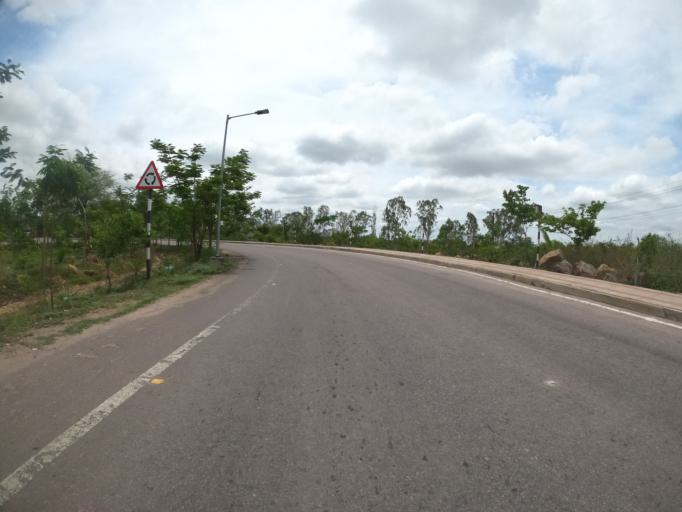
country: IN
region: Telangana
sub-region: Hyderabad
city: Hyderabad
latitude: 17.3496
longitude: 78.3622
